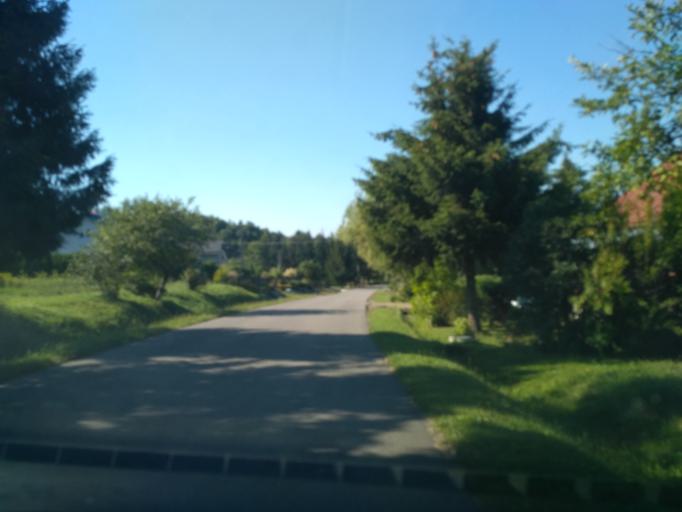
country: PL
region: Subcarpathian Voivodeship
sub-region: Powiat strzyzowski
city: Wysoka Strzyzowska
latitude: 49.8132
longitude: 21.7422
